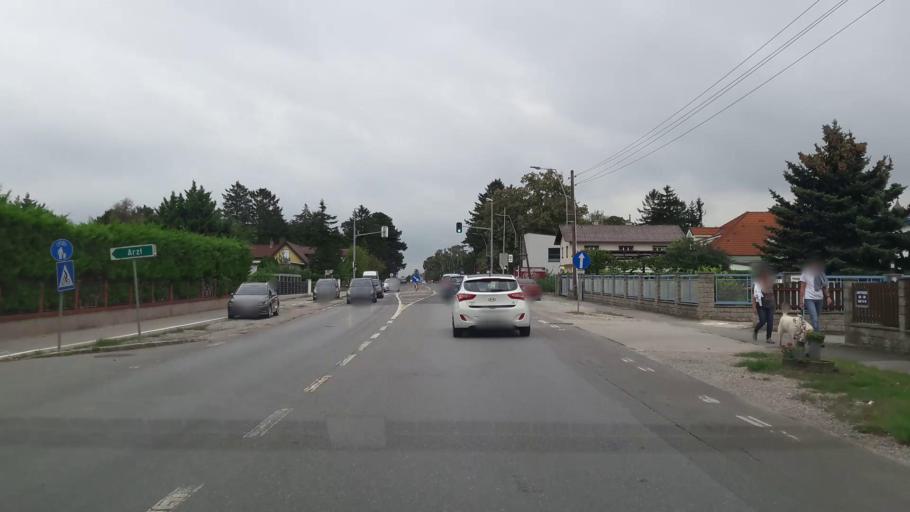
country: AT
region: Lower Austria
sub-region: Politischer Bezirk Ganserndorf
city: Strasshof an der Nordbahn
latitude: 48.3213
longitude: 16.6706
